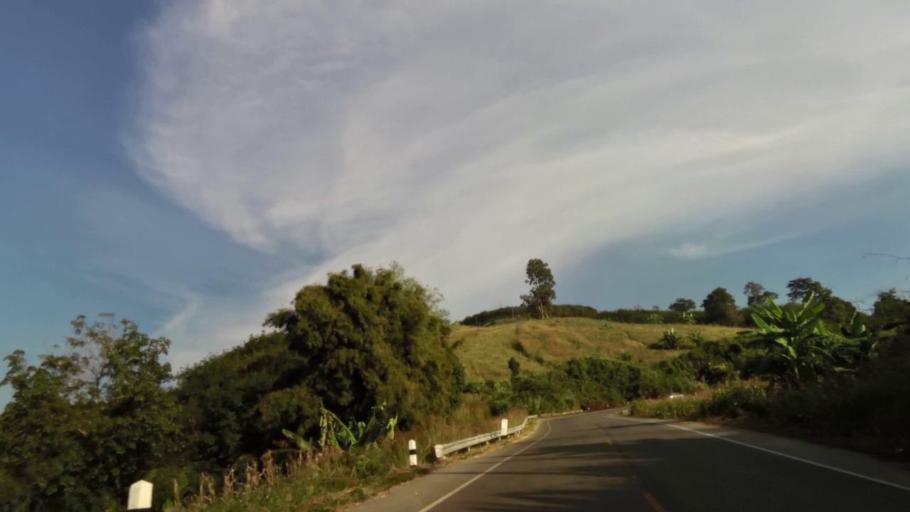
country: TH
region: Chiang Rai
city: Khun Tan
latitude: 19.8662
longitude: 100.4169
